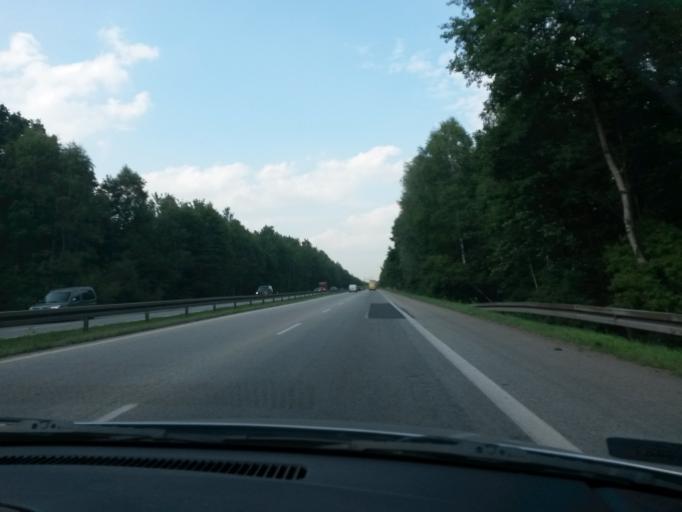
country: PL
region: Silesian Voivodeship
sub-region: Dabrowa Gornicza
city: Dabrowa Gornicza
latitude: 50.3011
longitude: 19.2232
